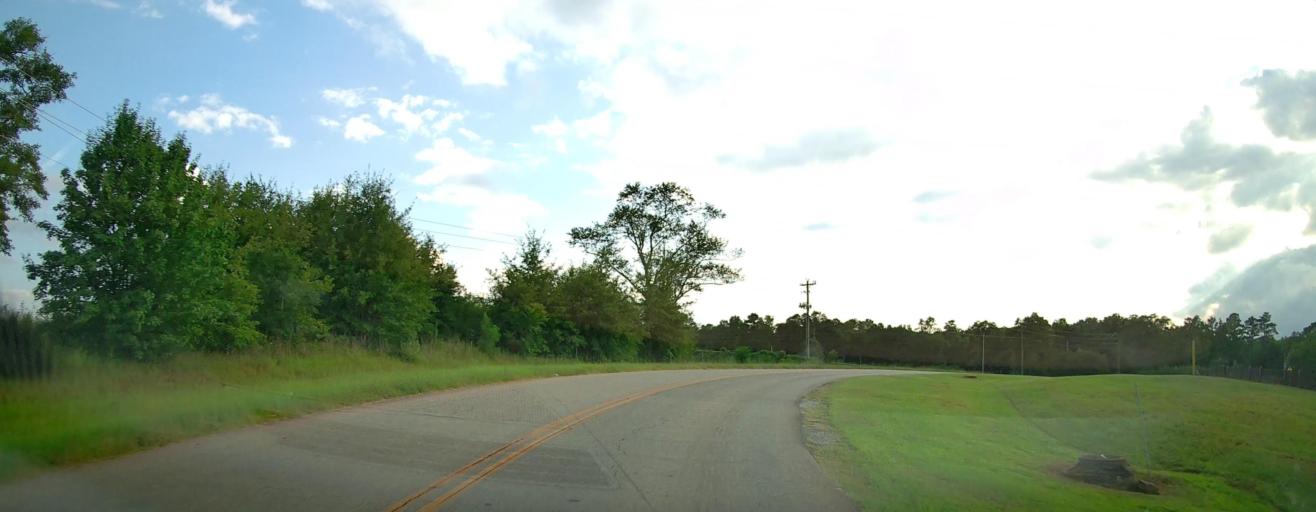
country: US
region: Georgia
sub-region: Monroe County
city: Forsyth
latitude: 33.0187
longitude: -83.9129
